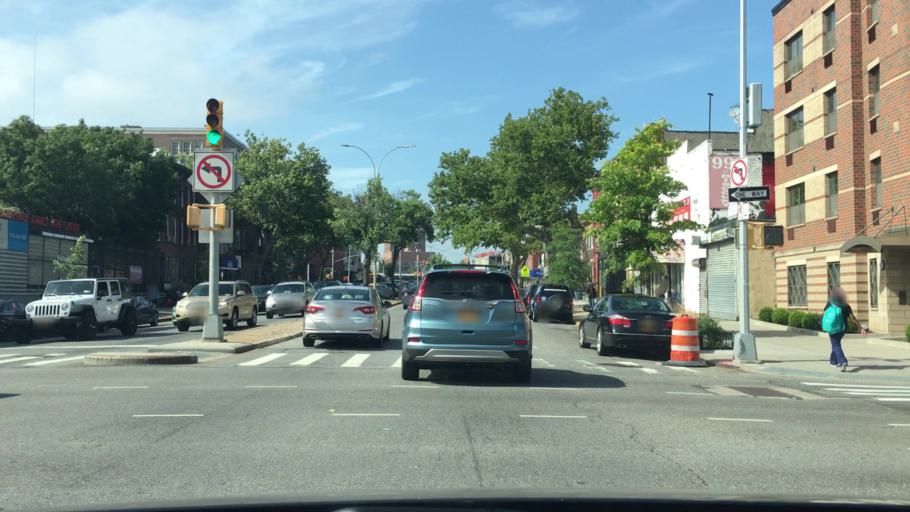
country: US
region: New York
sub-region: Kings County
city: East New York
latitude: 40.6762
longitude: -73.9080
